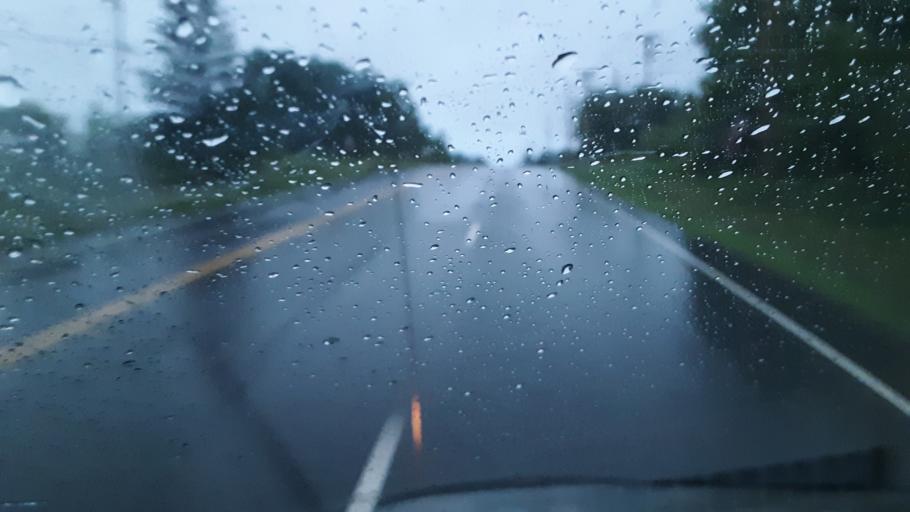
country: US
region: Maine
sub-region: Penobscot County
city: Patten
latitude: 45.9890
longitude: -68.4494
